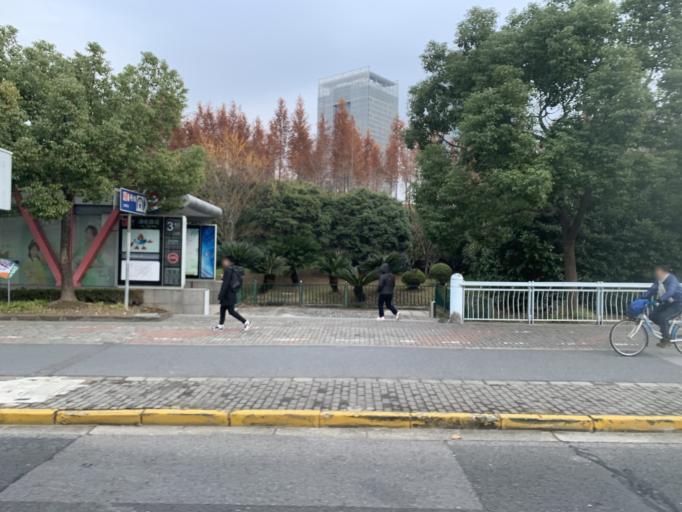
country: CN
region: Shanghai Shi
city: Pudong
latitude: 31.2217
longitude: 121.5248
